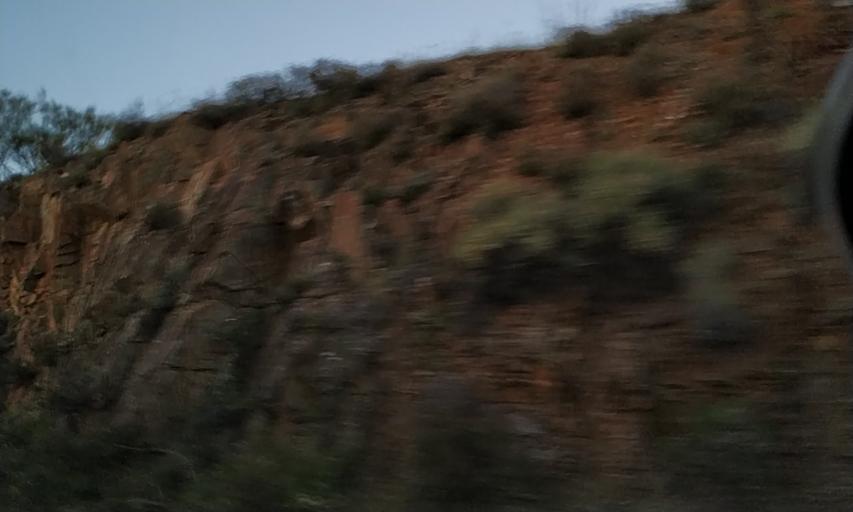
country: ES
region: Extremadura
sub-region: Provincia de Caceres
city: Alcantara
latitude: 39.7350
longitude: -6.9081
